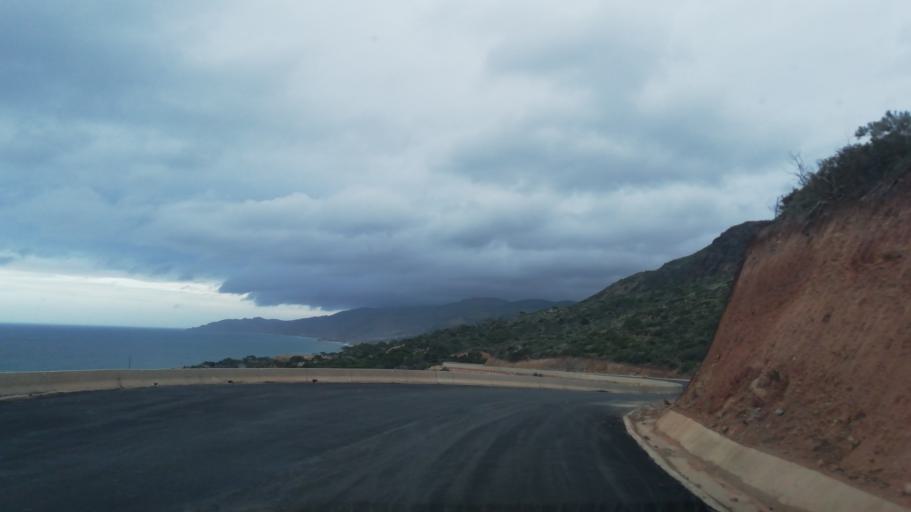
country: DZ
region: Oran
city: Bir el Djir
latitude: 35.7731
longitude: -0.5157
